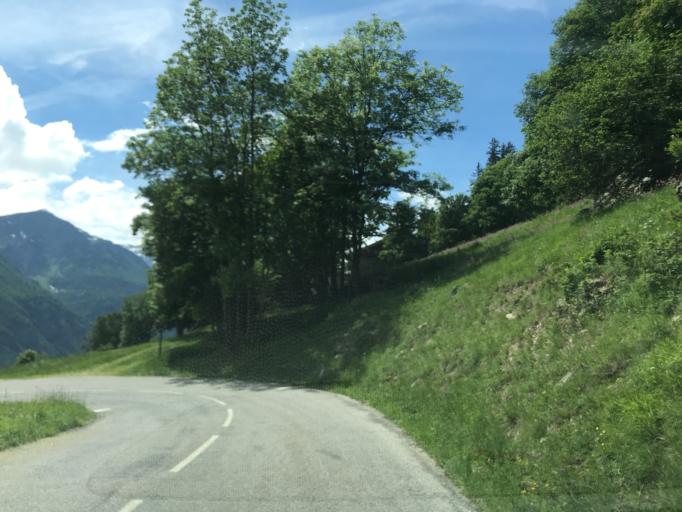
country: FR
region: Rhone-Alpes
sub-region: Departement de la Savoie
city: Modane
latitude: 45.2093
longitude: 6.6329
